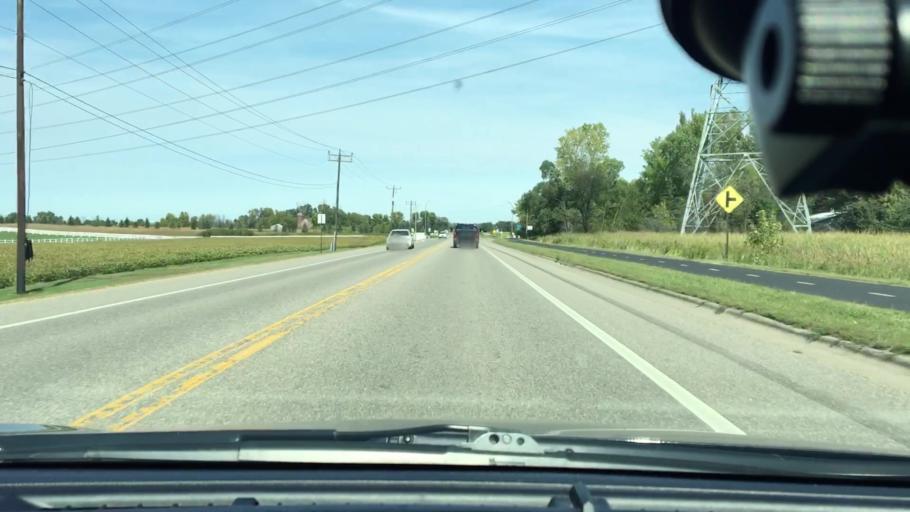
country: US
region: Minnesota
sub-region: Wright County
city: Hanover
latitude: 45.1284
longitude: -93.6357
